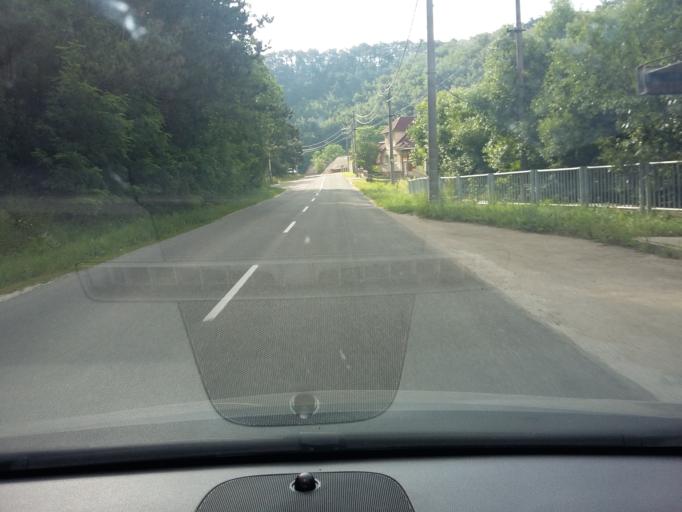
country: SK
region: Trnavsky
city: Smolenice
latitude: 48.5427
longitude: 17.4055
